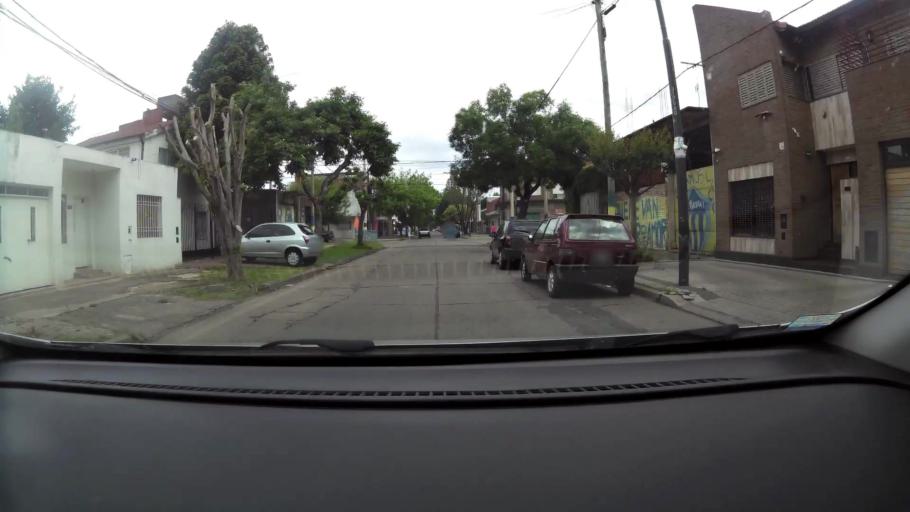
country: AR
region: Santa Fe
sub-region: Departamento de Rosario
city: Rosario
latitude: -32.9727
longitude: -60.6535
